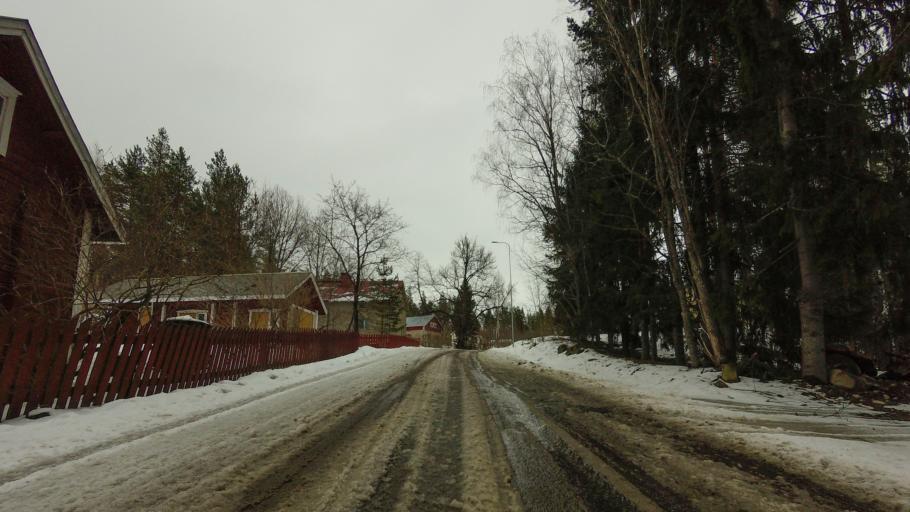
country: FI
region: Southern Savonia
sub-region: Savonlinna
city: Rantasalmi
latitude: 62.1127
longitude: 28.6085
